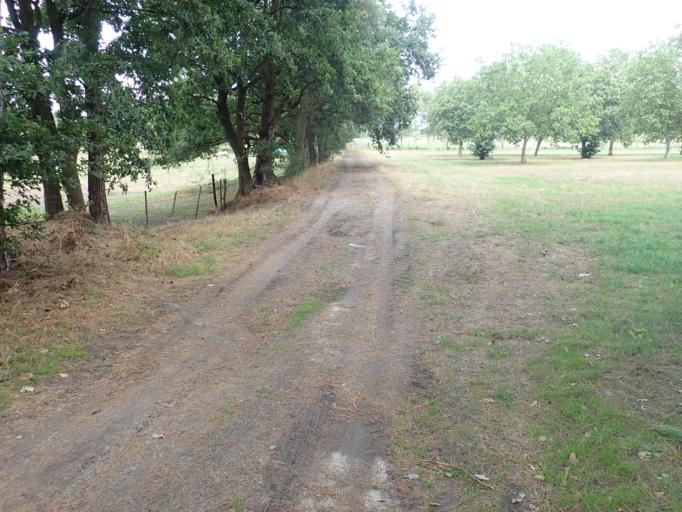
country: BE
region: Flanders
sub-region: Provincie Antwerpen
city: Meerhout
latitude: 51.1565
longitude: 5.0918
